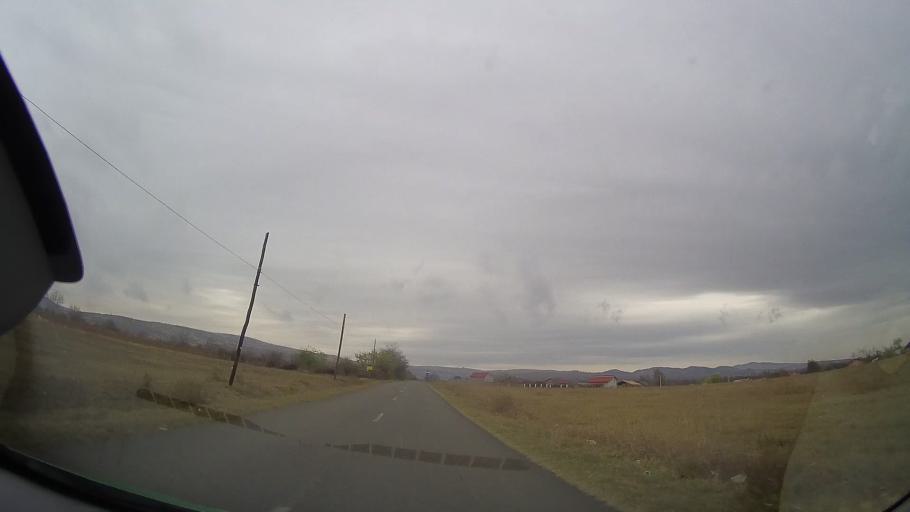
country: RO
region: Prahova
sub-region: Comuna Vadu Sapat
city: Vadu Sapat
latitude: 45.0260
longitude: 26.3832
